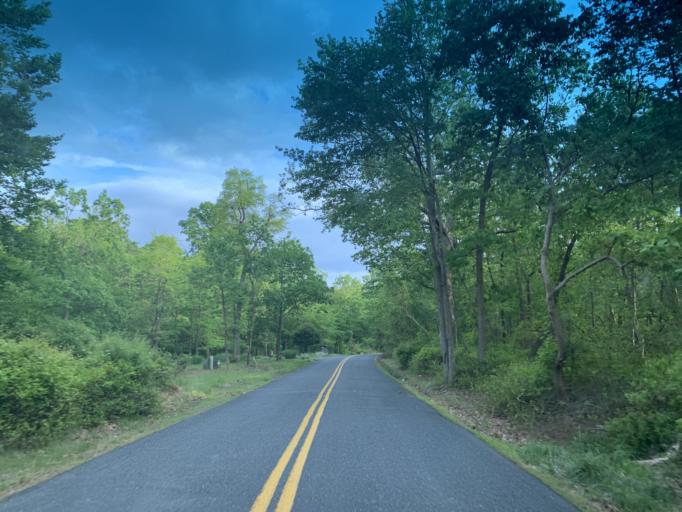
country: US
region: Pennsylvania
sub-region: York County
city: Susquehanna Trails
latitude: 39.6884
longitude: -76.2431
